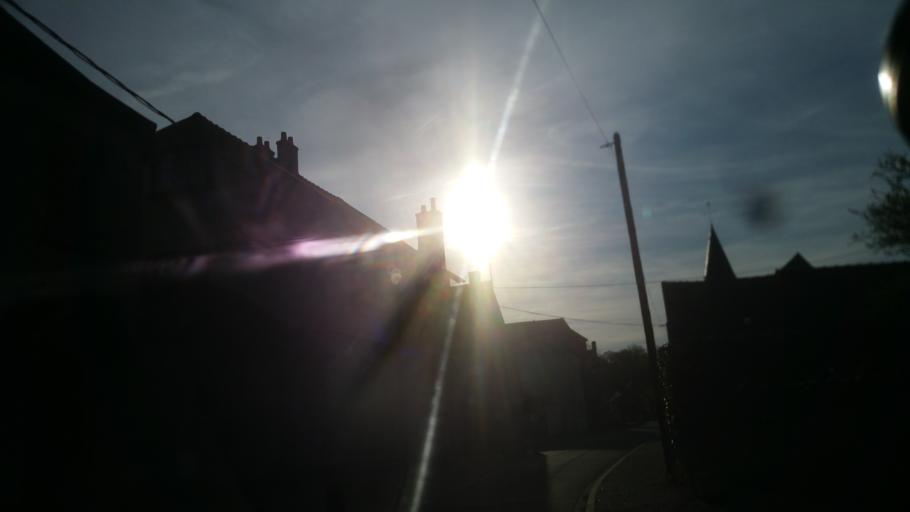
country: FR
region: Ile-de-France
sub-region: Departement de l'Essonne
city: Le Val-Saint-Germain
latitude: 48.5654
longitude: 2.0631
